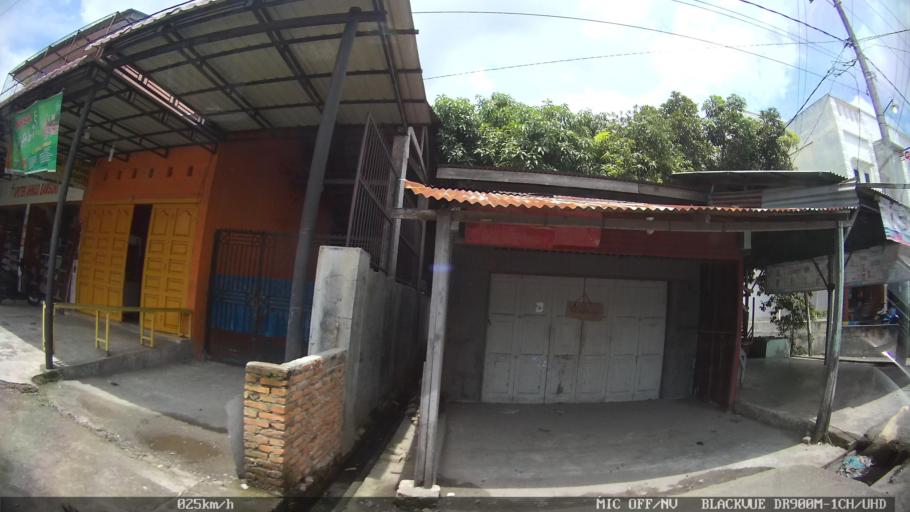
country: ID
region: North Sumatra
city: Medan
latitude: 3.6143
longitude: 98.7480
